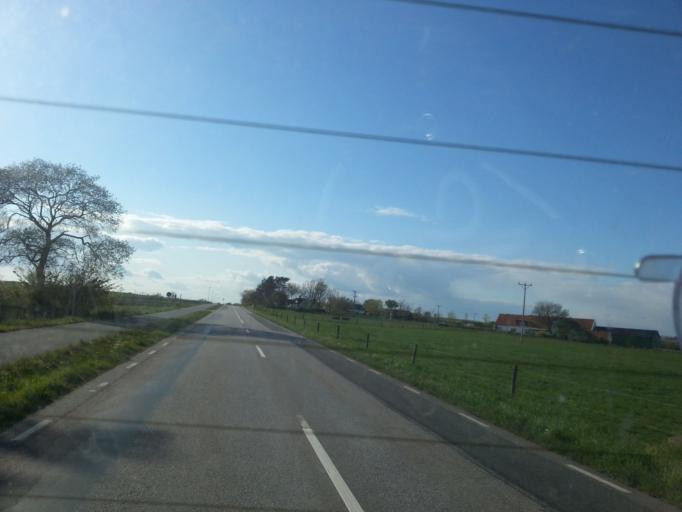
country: SE
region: Skane
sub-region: Ystads Kommun
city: Kopingebro
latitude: 55.4278
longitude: 13.9833
